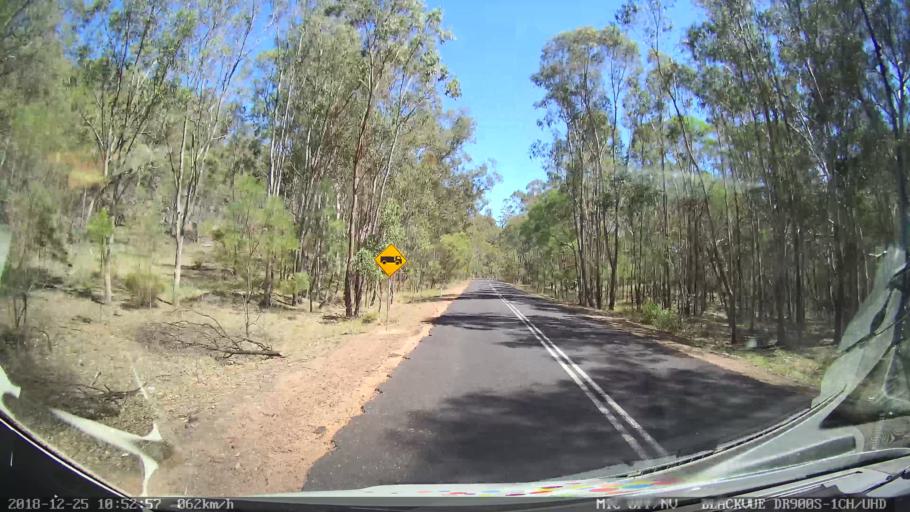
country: AU
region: New South Wales
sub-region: Upper Hunter Shire
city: Merriwa
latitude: -32.4241
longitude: 150.2736
